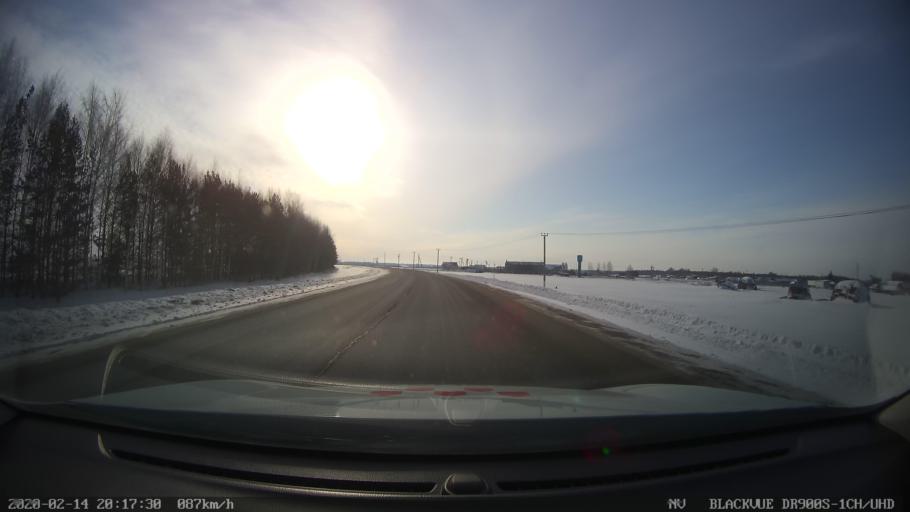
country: RU
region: Tatarstan
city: Verkhniy Uslon
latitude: 55.5990
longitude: 48.8778
